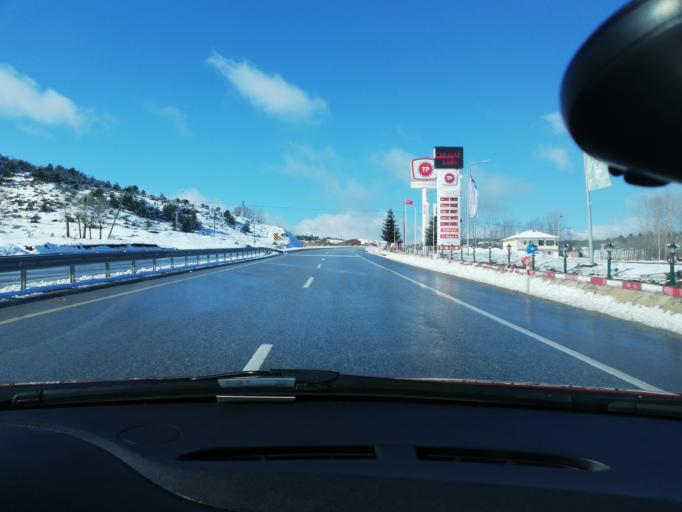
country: TR
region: Kastamonu
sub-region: Cide
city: Kastamonu
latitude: 41.3558
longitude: 33.6674
